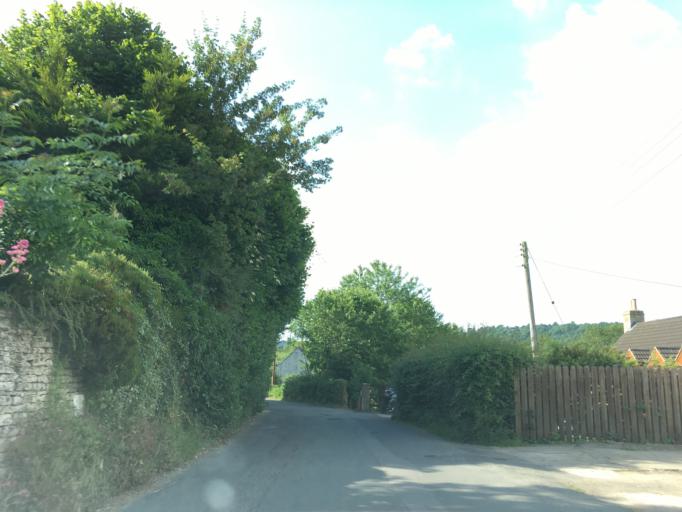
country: GB
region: England
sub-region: Gloucestershire
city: Stroud
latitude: 51.7323
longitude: -2.2012
